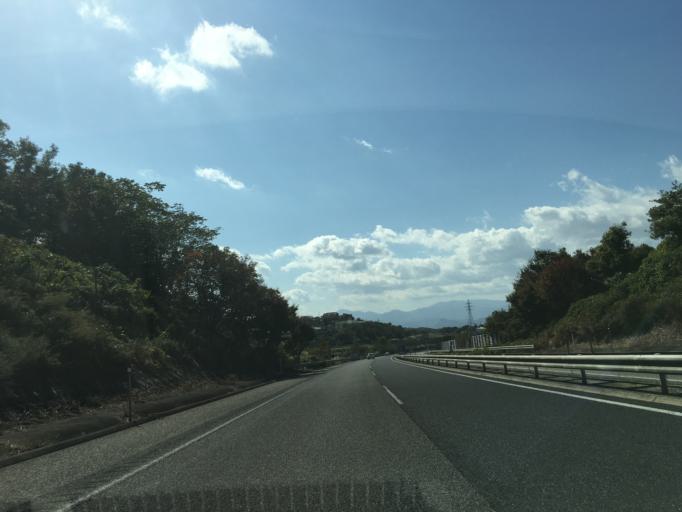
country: JP
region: Fukushima
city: Kitakata
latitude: 37.5384
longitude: 139.9556
